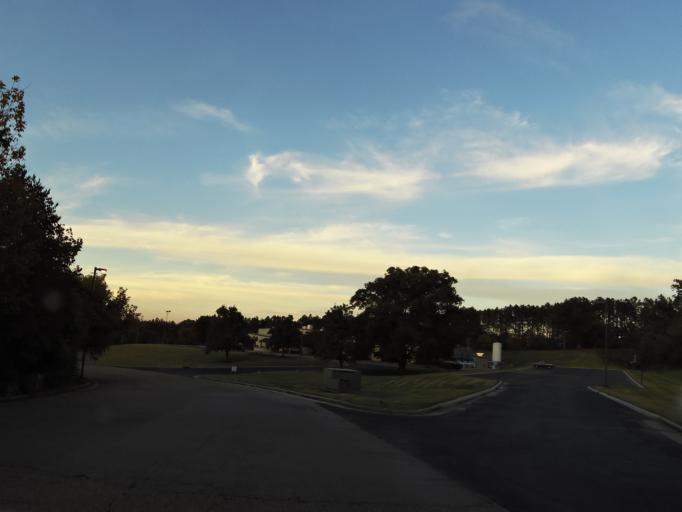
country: US
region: Tennessee
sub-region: Blount County
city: Eagleton Village
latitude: 35.8638
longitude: -83.9333
